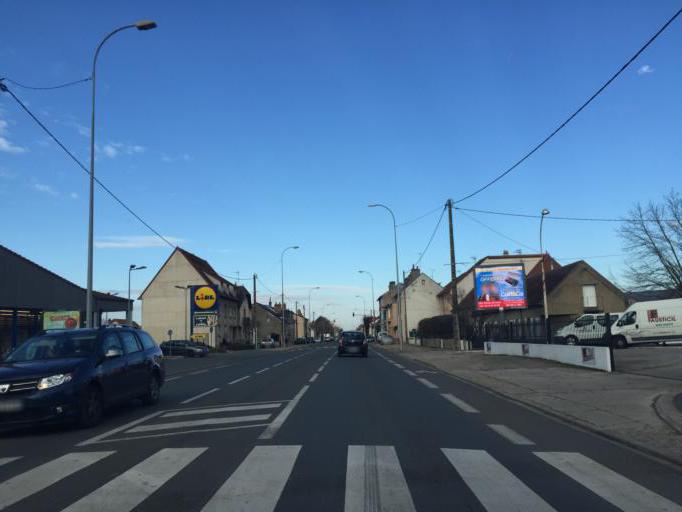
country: FR
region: Auvergne
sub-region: Departement de l'Allier
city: Moulins
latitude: 46.5514
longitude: 3.3382
